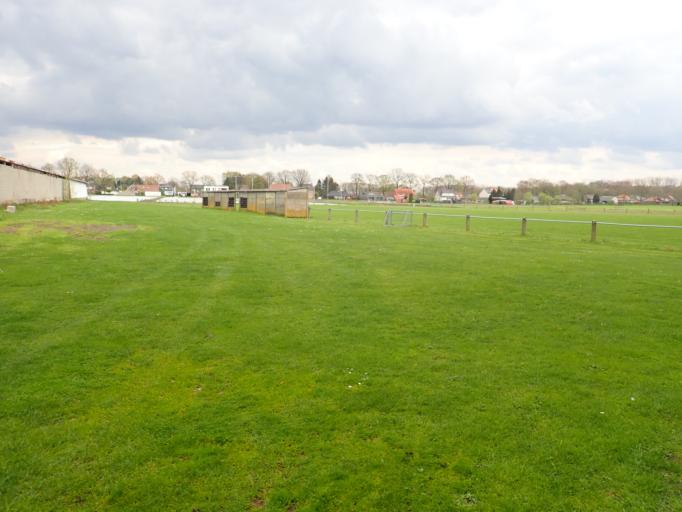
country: BE
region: Flanders
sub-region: Provincie Antwerpen
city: Lille
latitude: 51.2213
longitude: 4.8351
